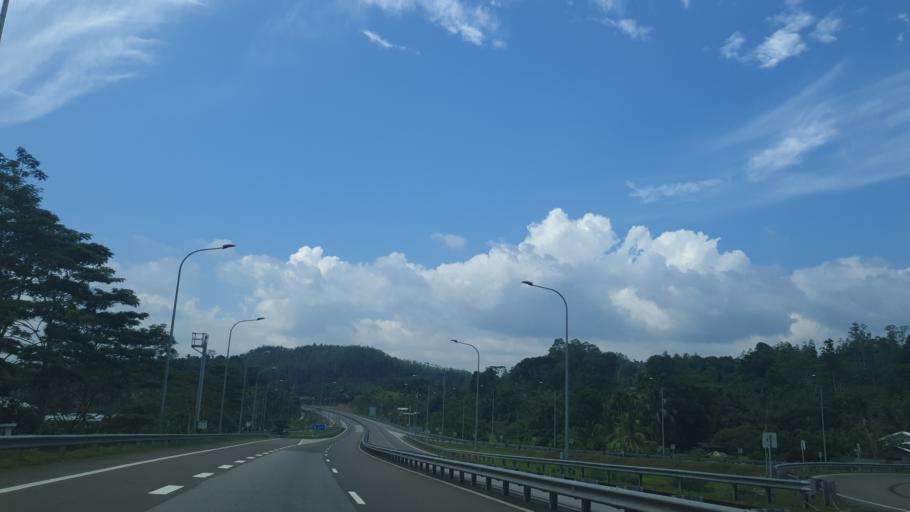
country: LK
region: Southern
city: Weligama
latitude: 6.0351
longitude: 80.3658
